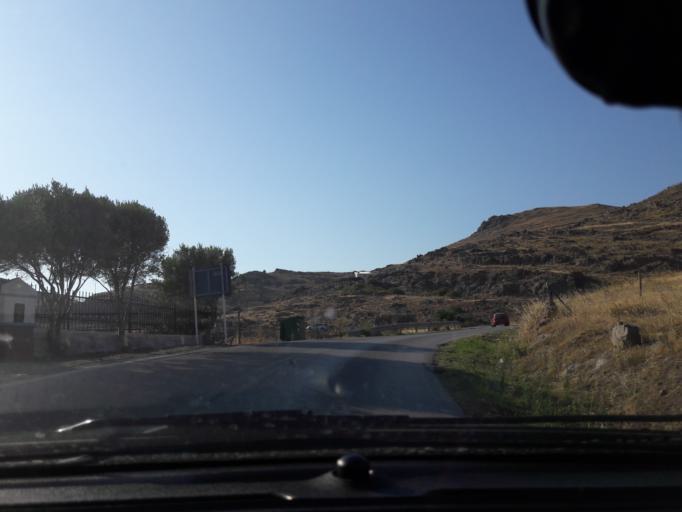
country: GR
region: North Aegean
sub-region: Nomos Lesvou
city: Myrina
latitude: 39.8587
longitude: 25.0835
